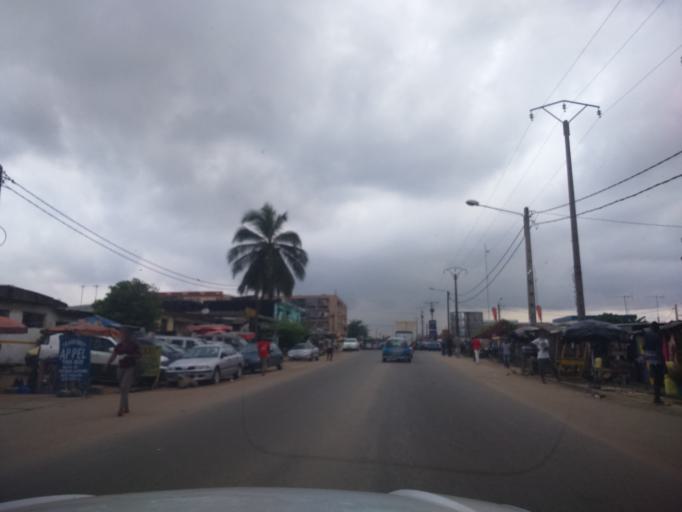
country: CI
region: Lagunes
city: Abidjan
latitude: 5.3467
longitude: -4.0651
